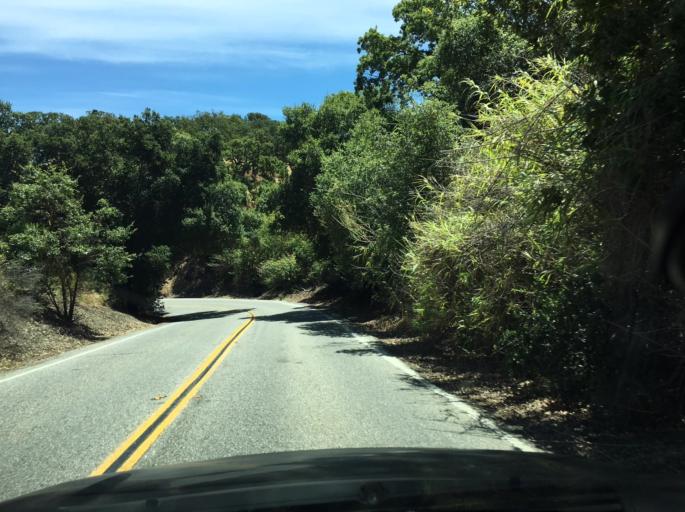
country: US
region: California
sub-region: Santa Clara County
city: Morgan Hill
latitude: 37.1842
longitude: -121.7561
